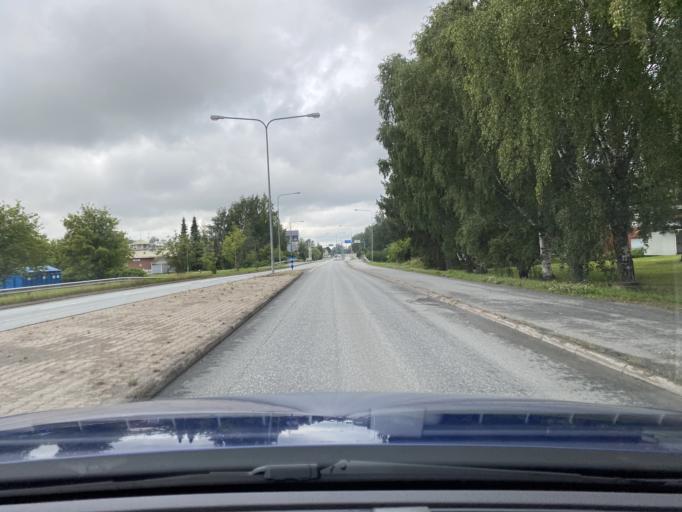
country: FI
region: Ostrobothnia
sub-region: Kyroenmaa
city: Laihia
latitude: 62.9785
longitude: 22.0127
